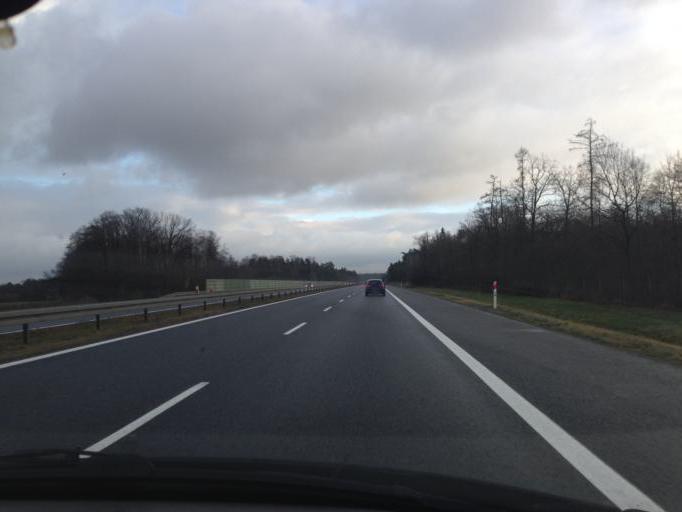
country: PL
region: Silesian Voivodeship
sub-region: Powiat gliwicki
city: Rudziniec
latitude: 50.3739
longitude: 18.4838
